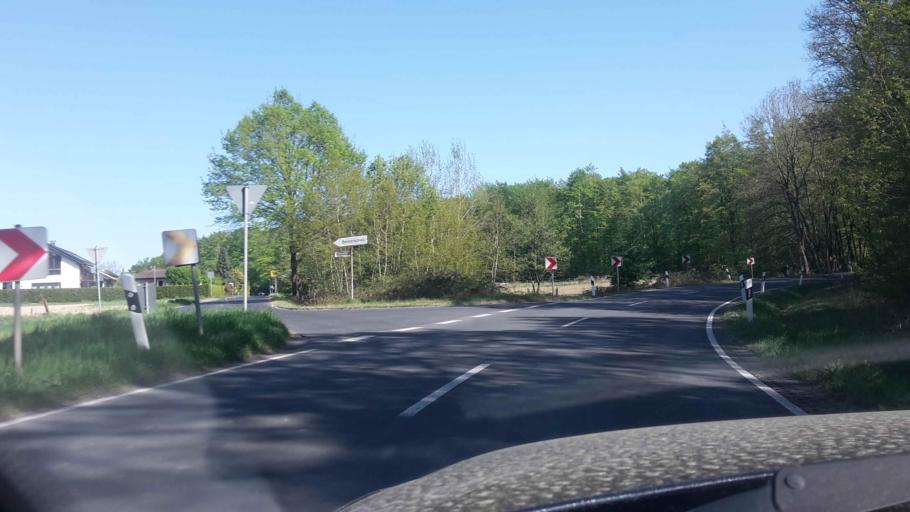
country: DE
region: North Rhine-Westphalia
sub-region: Regierungsbezirk Koln
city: Hennef
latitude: 50.7067
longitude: 7.3163
